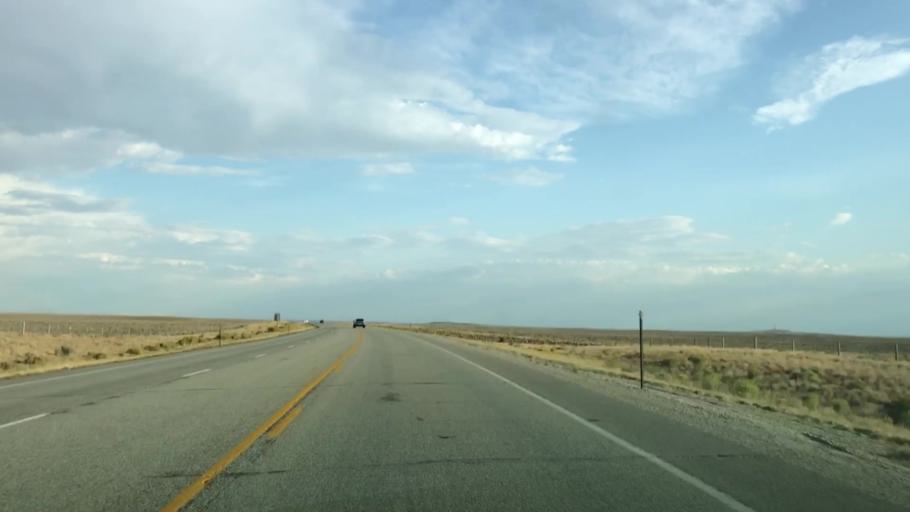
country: US
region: Wyoming
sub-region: Sublette County
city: Pinedale
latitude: 42.4133
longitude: -109.5539
